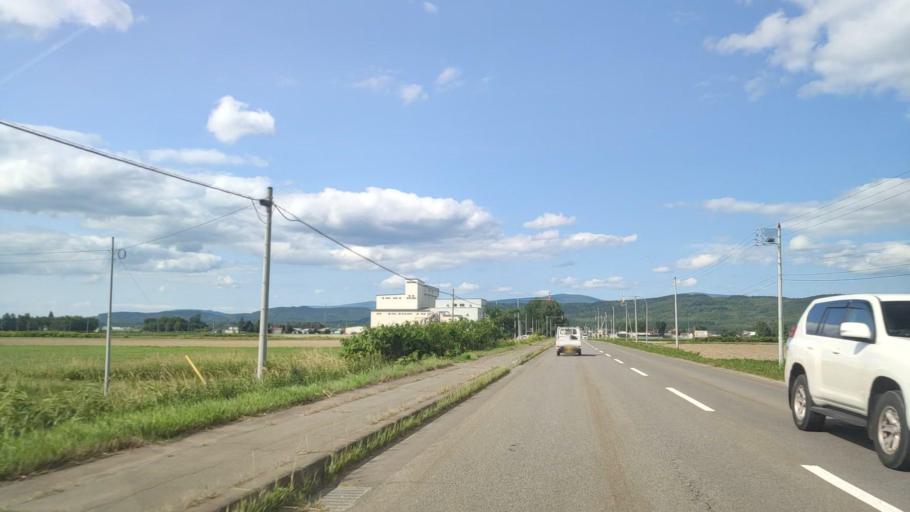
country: JP
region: Hokkaido
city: Nayoro
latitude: 44.4304
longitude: 142.4006
